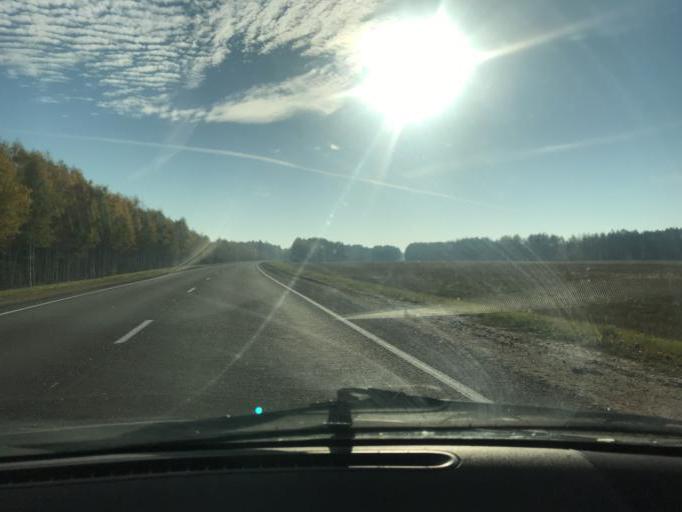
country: BY
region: Brest
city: Drahichyn
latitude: 52.1866
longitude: 25.2878
